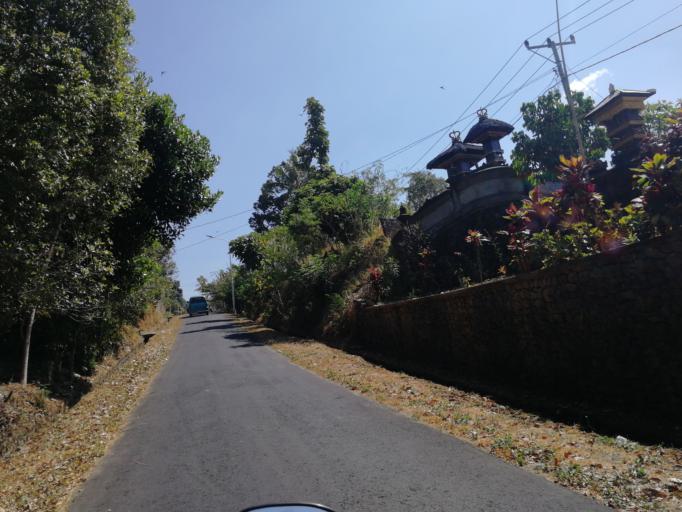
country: ID
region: Bali
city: Banjar Kedisan
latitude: -8.1567
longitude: 115.3067
